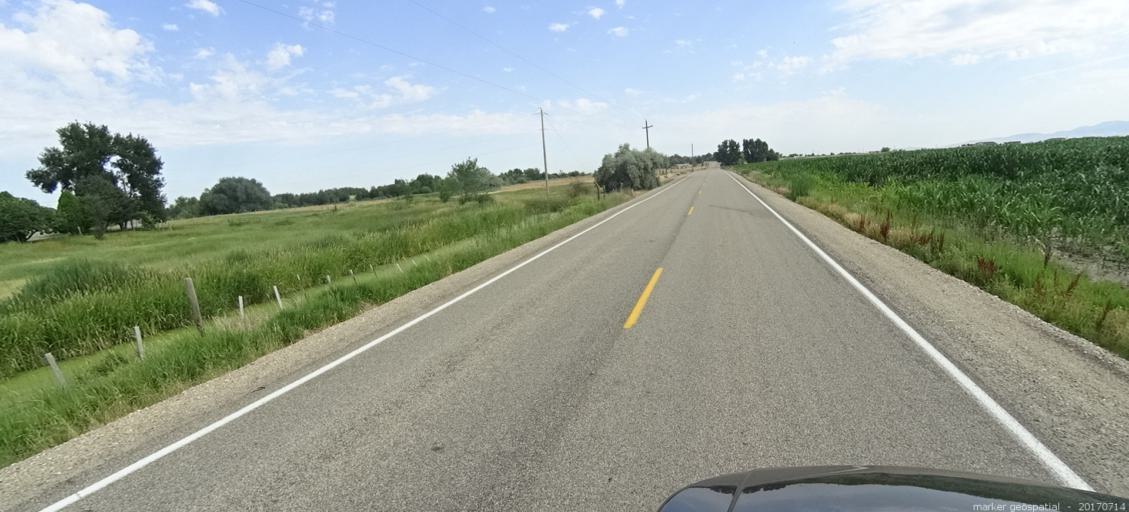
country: US
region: Idaho
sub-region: Ada County
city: Kuna
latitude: 43.4783
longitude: -116.3544
